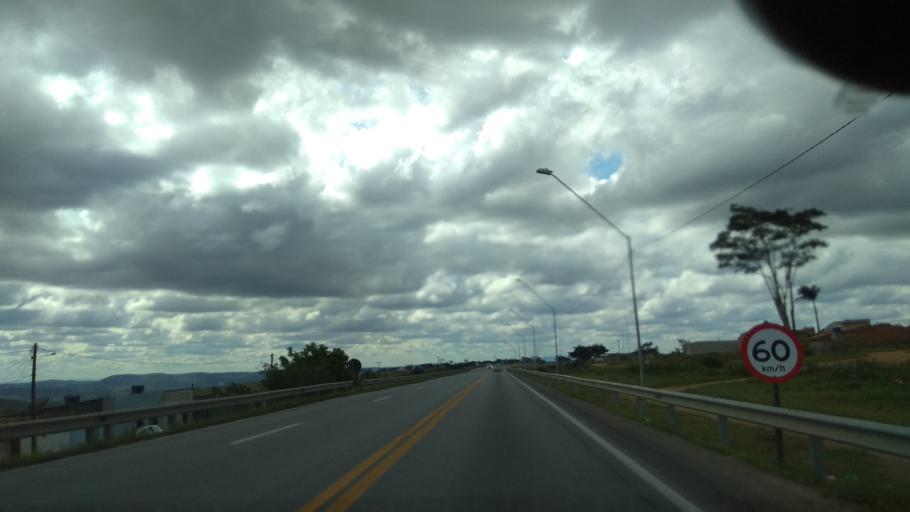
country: BR
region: Bahia
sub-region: Santa Ines
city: Santa Ines
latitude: -13.0705
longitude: -39.9609
